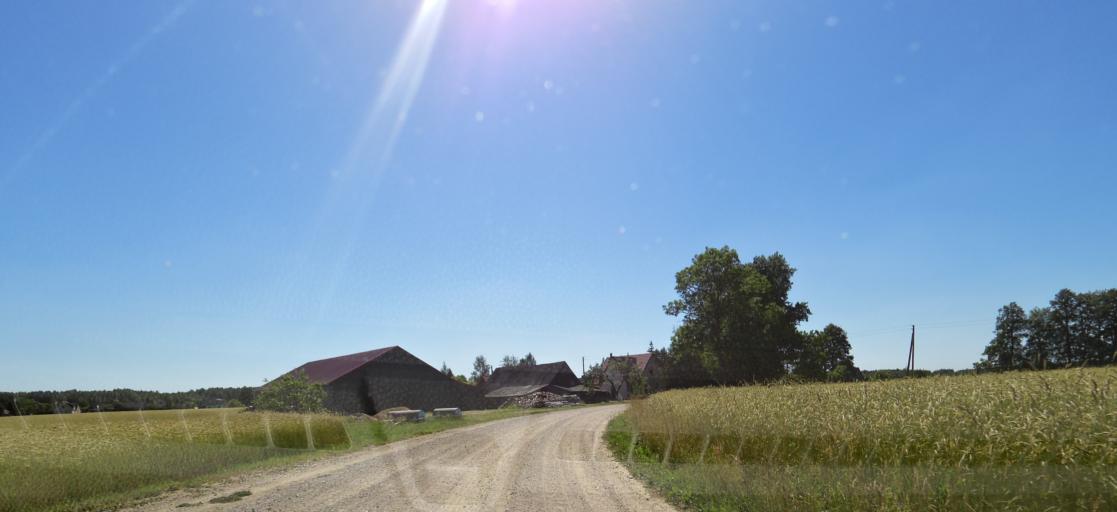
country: LT
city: Vabalninkas
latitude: 55.9342
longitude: 24.6543
